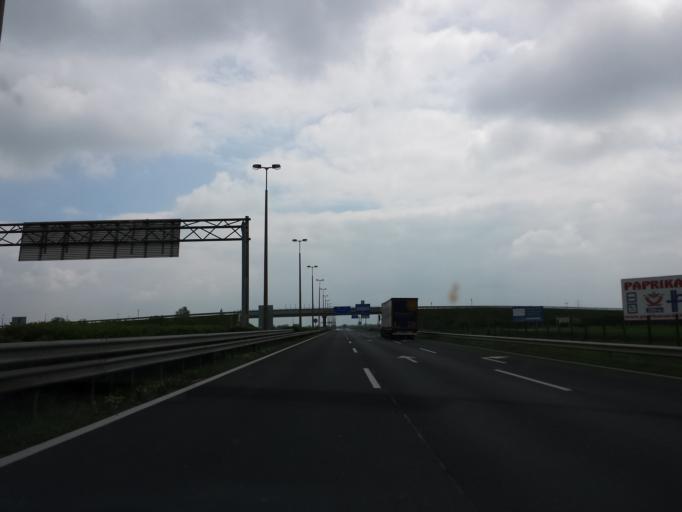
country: AT
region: Burgenland
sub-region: Politischer Bezirk Neusiedl am See
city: Nickelsdorf
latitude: 47.9174
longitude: 17.1221
